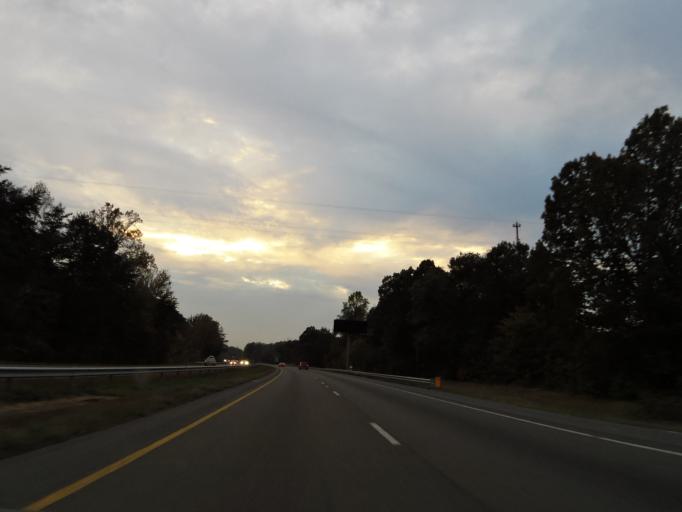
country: US
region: North Carolina
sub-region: Burke County
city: Drexel
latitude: 35.7310
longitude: -81.6084
